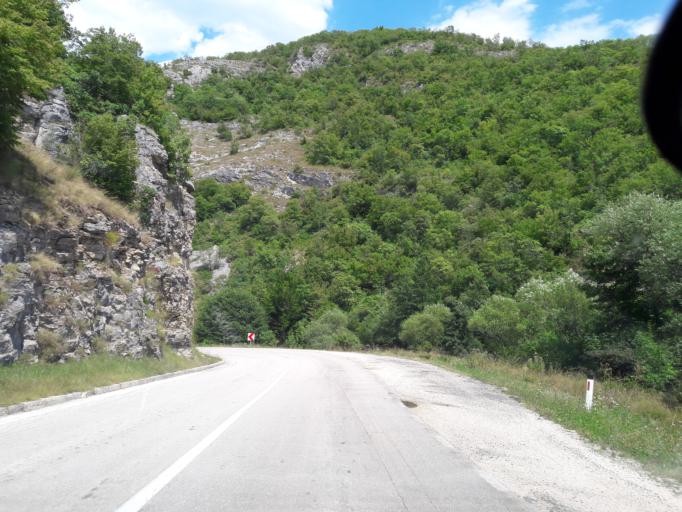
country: BA
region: Republika Srpska
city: Mrkonjic Grad
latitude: 44.4556
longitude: 17.1607
